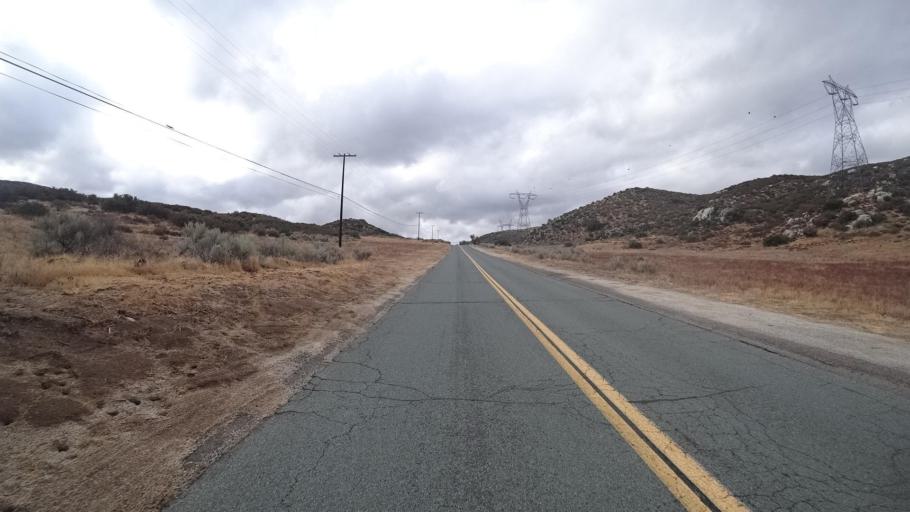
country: US
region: California
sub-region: San Diego County
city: Campo
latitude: 32.7140
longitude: -116.4302
